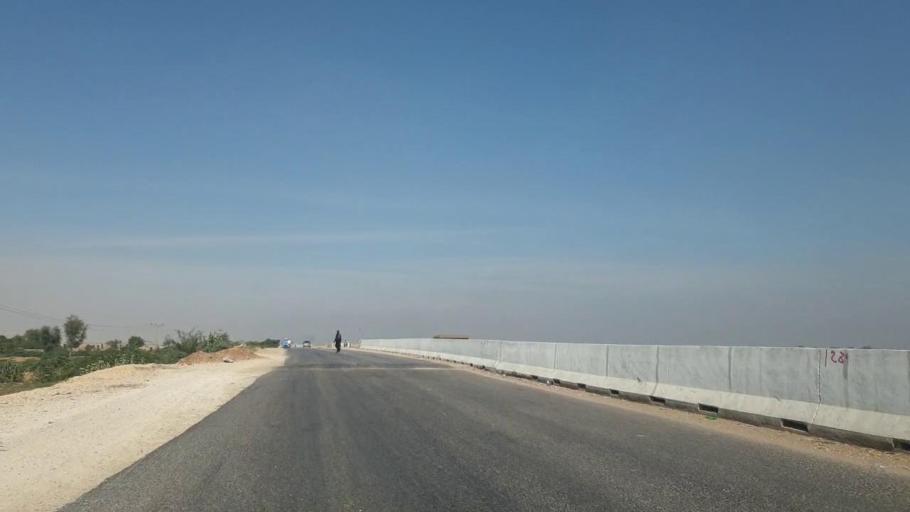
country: PK
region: Sindh
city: Matiari
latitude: 25.6517
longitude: 68.3008
